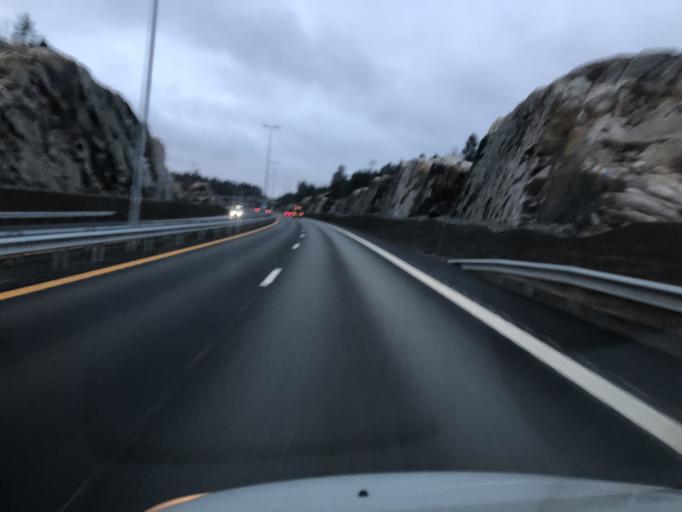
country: NO
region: Aust-Agder
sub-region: Arendal
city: Arendal
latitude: 58.5131
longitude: 8.8237
